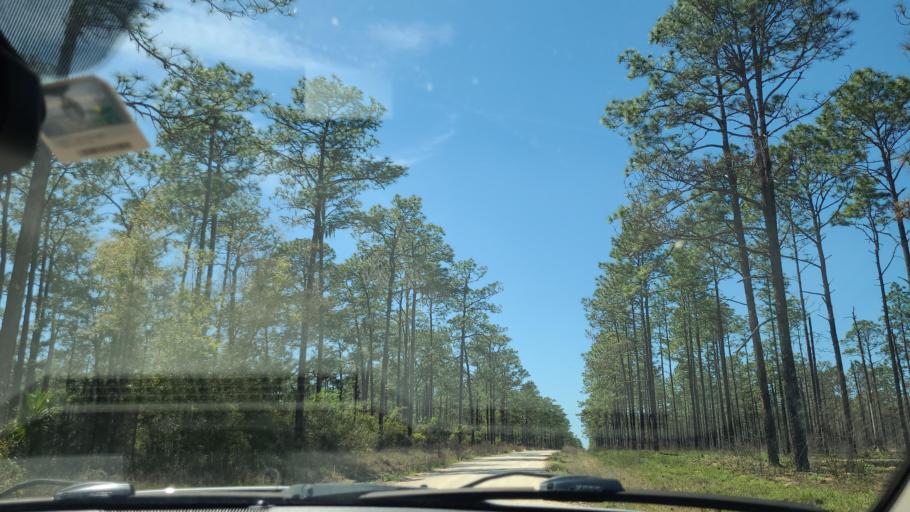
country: US
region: Florida
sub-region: Putnam County
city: Interlachen
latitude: 29.4290
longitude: -81.7915
